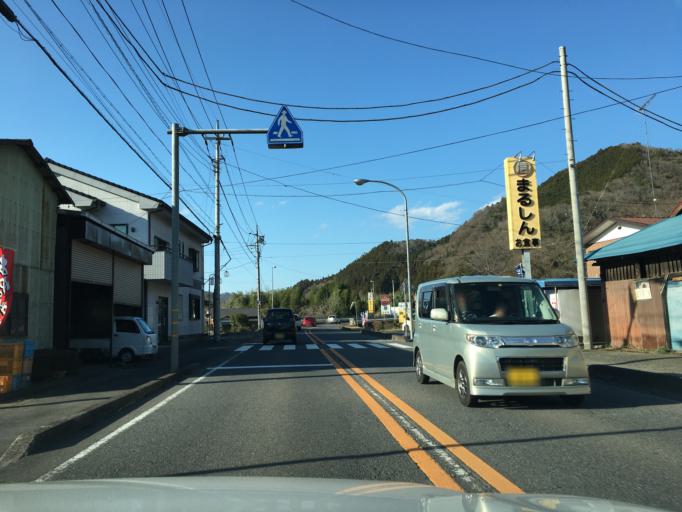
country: JP
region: Ibaraki
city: Omiya
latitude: 36.6540
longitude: 140.3931
